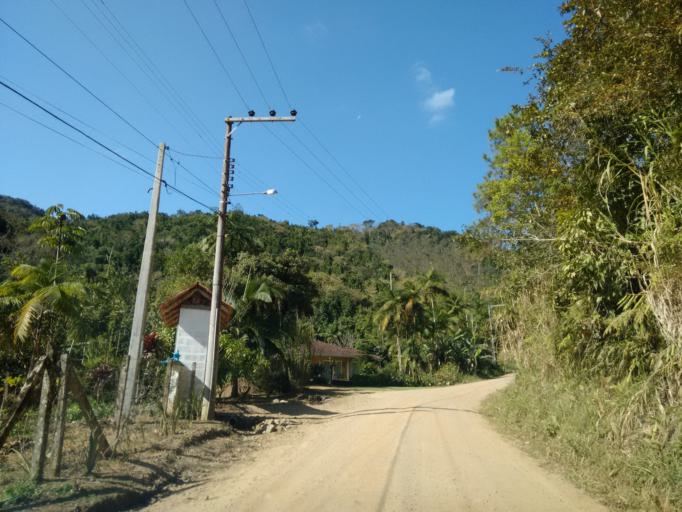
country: BR
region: Santa Catarina
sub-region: Pomerode
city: Pomerode
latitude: -26.7404
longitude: -49.1589
